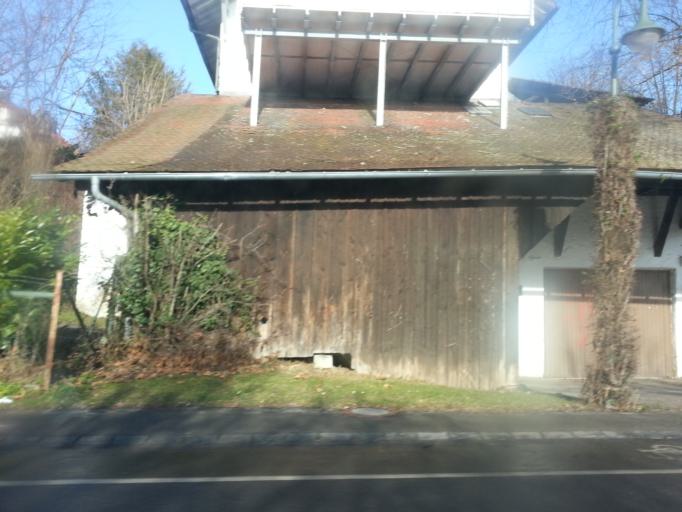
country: DE
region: Baden-Wuerttemberg
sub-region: Tuebingen Region
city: Immenstaad am Bodensee
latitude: 47.6665
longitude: 9.3768
